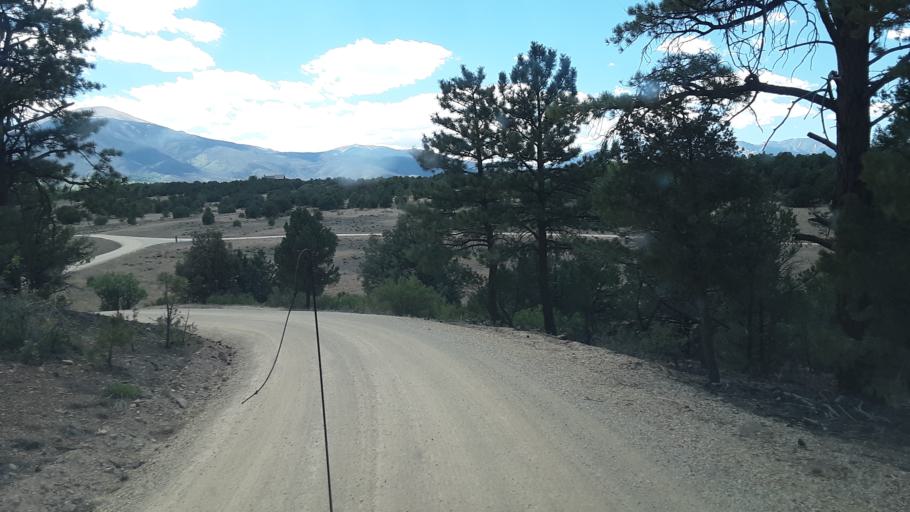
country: US
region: Colorado
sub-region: Custer County
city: Westcliffe
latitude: 38.3145
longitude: -105.6314
